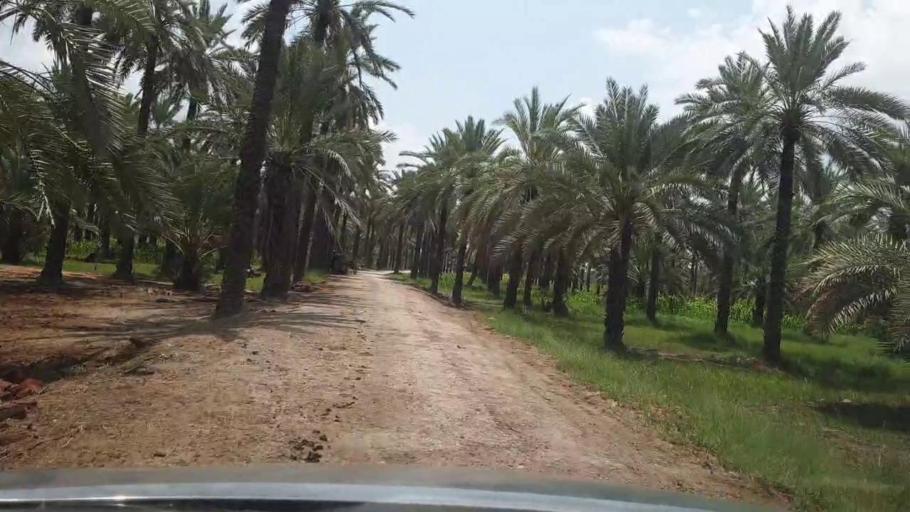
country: PK
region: Sindh
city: Khairpur
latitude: 27.6331
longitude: 68.7331
